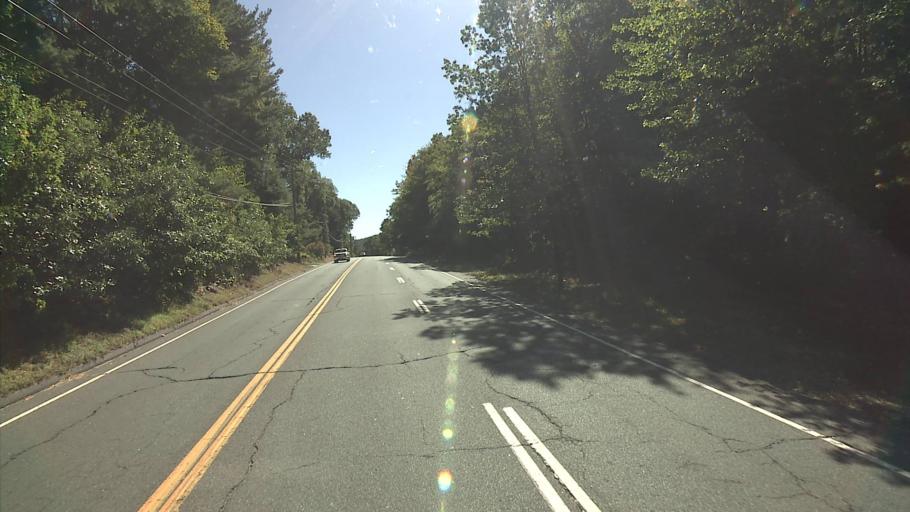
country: US
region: Connecticut
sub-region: New Haven County
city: Prospect
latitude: 41.5285
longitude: -73.0046
